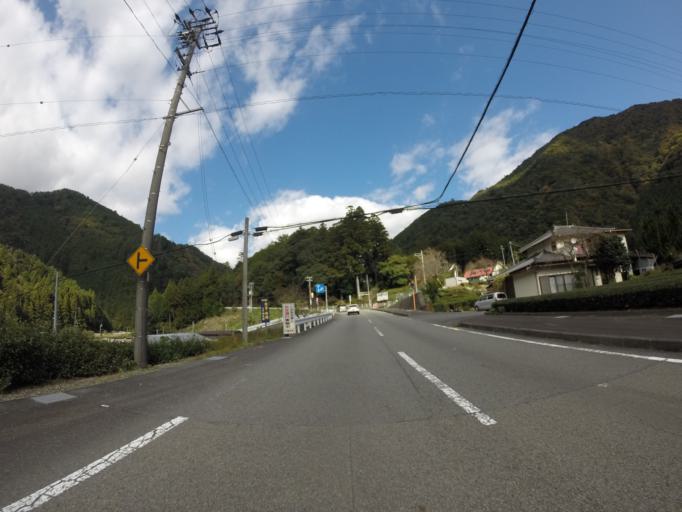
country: JP
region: Shizuoka
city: Shizuoka-shi
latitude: 35.1514
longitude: 138.1459
